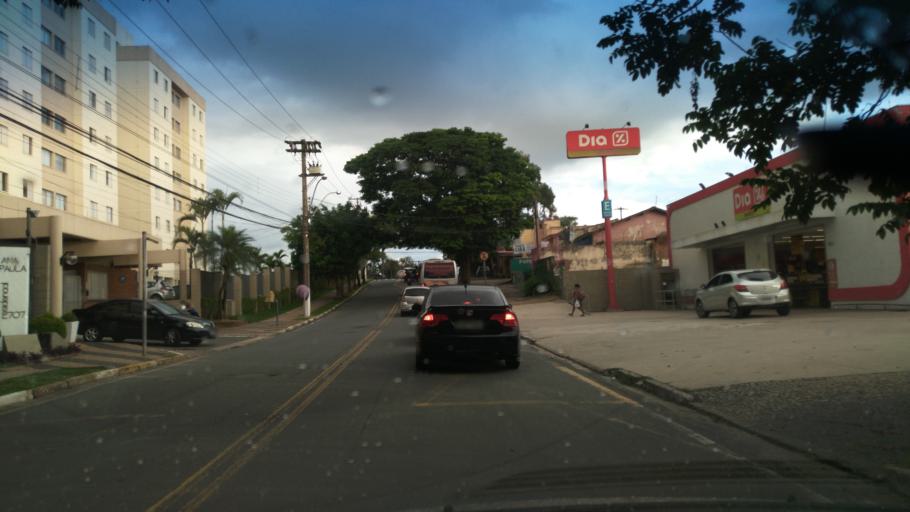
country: BR
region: Sao Paulo
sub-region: Campinas
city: Campinas
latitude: -22.9292
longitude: -47.0354
